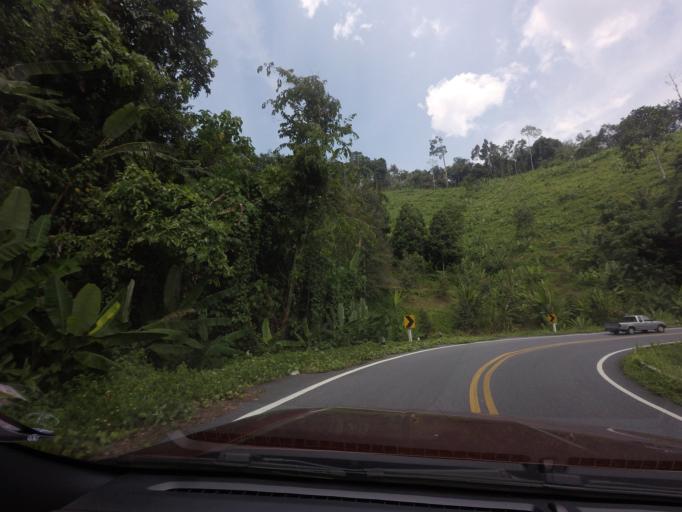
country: TH
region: Yala
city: Than To
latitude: 6.0388
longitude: 101.2085
